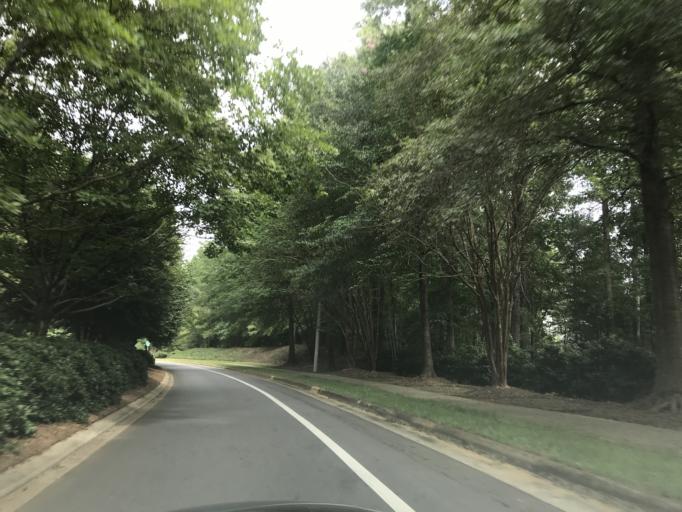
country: US
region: North Carolina
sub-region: Wake County
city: Cary
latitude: 35.7320
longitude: -78.7829
